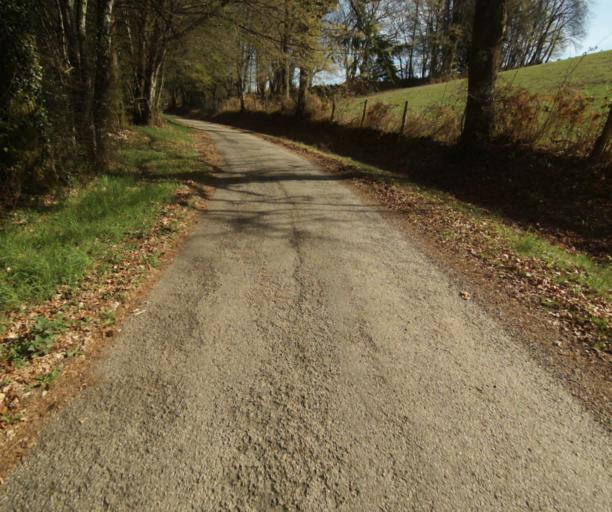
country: FR
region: Limousin
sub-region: Departement de la Correze
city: Naves
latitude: 45.3513
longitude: 1.7613
